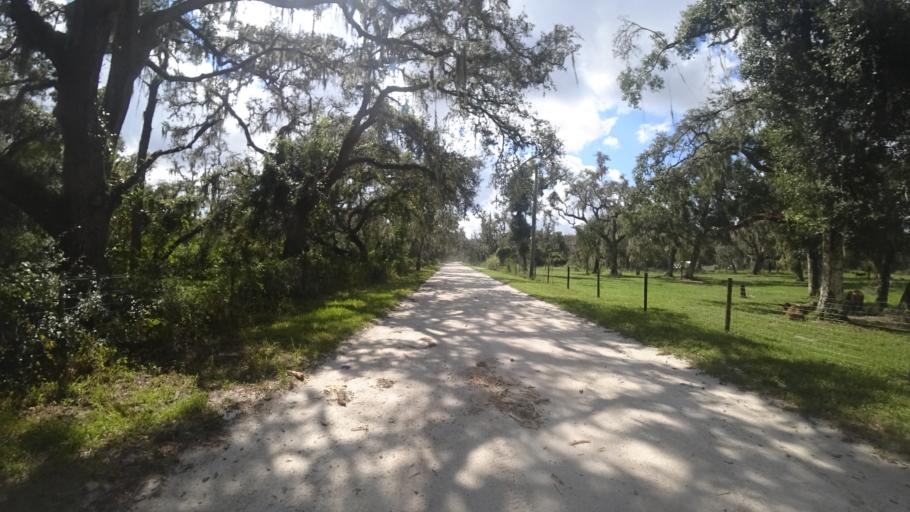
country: US
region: Florida
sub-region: Sarasota County
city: Lake Sarasota
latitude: 27.3881
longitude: -82.2191
